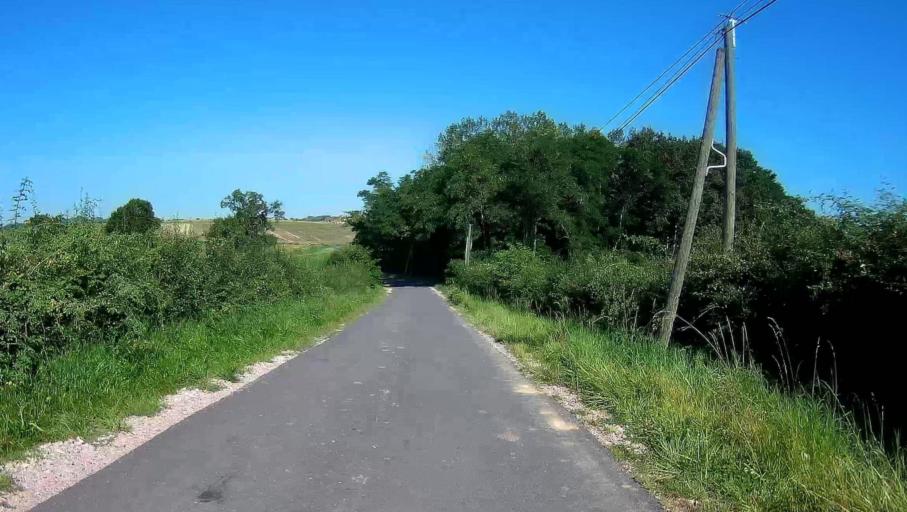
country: FR
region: Bourgogne
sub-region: Departement de Saone-et-Loire
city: Couches
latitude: 46.8373
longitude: 4.5851
